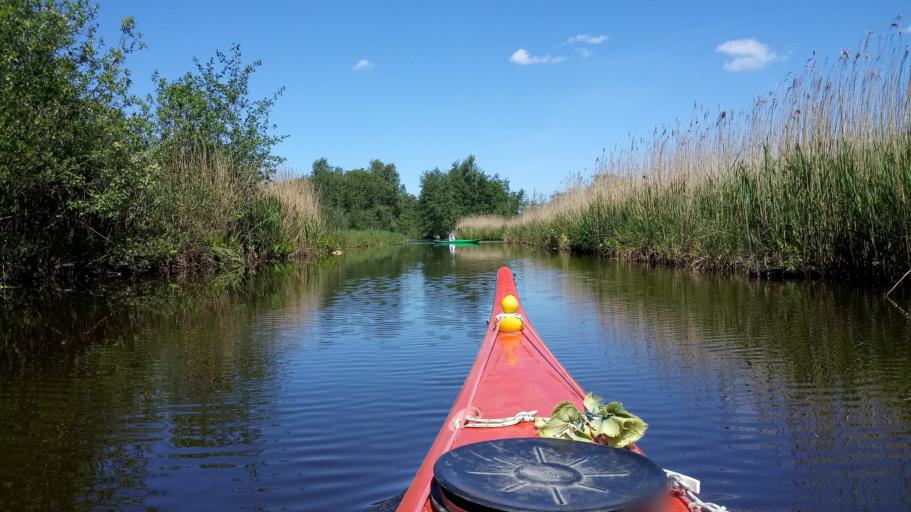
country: NL
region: South Holland
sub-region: Gemeente Nieuwkoop
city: Nieuwkoop
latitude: 52.1570
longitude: 4.8230
